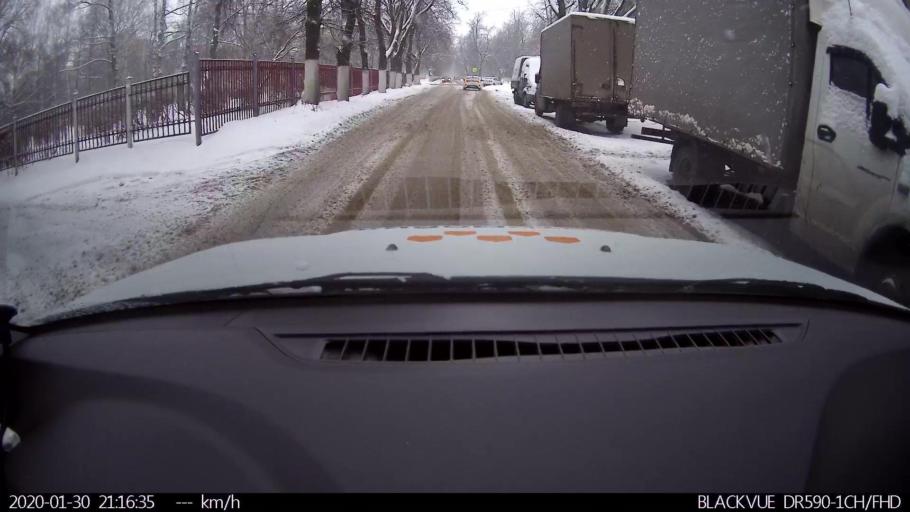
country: RU
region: Nizjnij Novgorod
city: Gorbatovka
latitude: 56.2467
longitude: 43.8539
